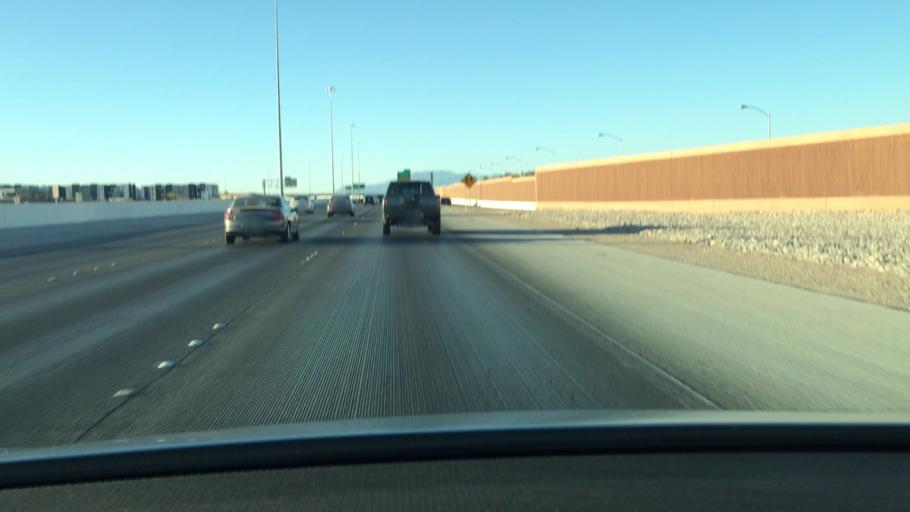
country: US
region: Nevada
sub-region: Clark County
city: Spring Valley
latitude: 36.0874
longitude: -115.2887
